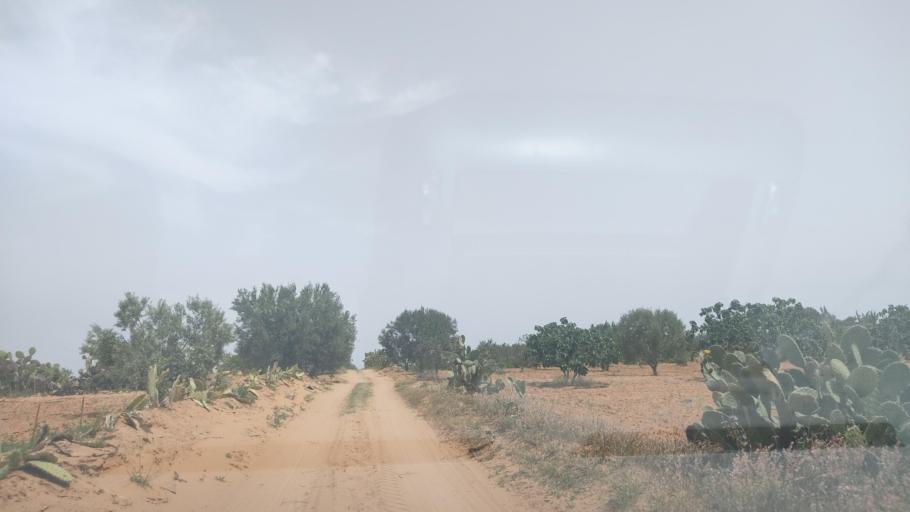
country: TN
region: Safaqis
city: Sfax
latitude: 34.8450
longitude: 10.5929
